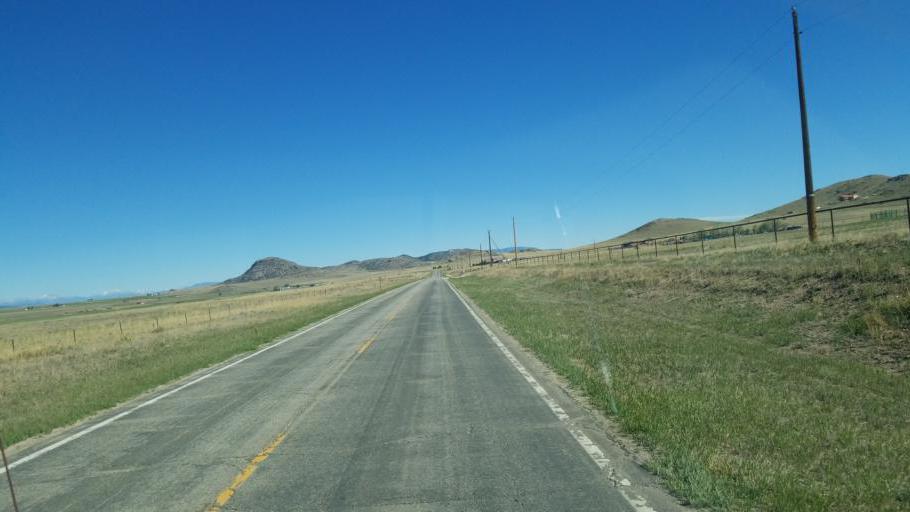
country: US
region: Colorado
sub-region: Custer County
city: Westcliffe
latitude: 38.1534
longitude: -105.4790
